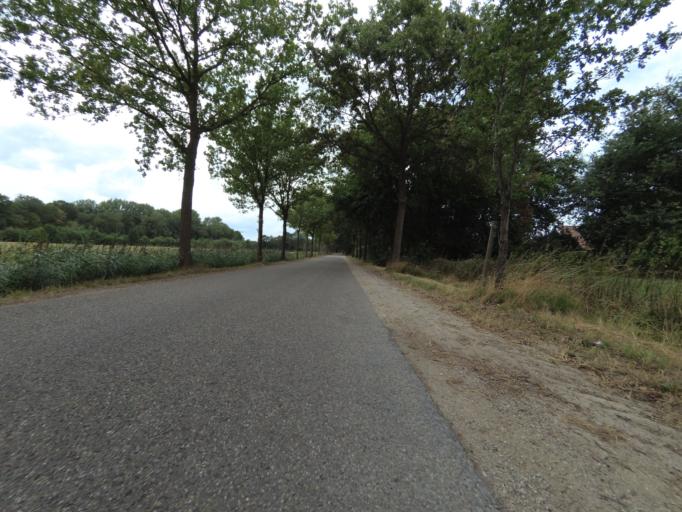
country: NL
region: Overijssel
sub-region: Gemeente Enschede
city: Enschede
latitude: 52.2029
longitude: 6.9394
